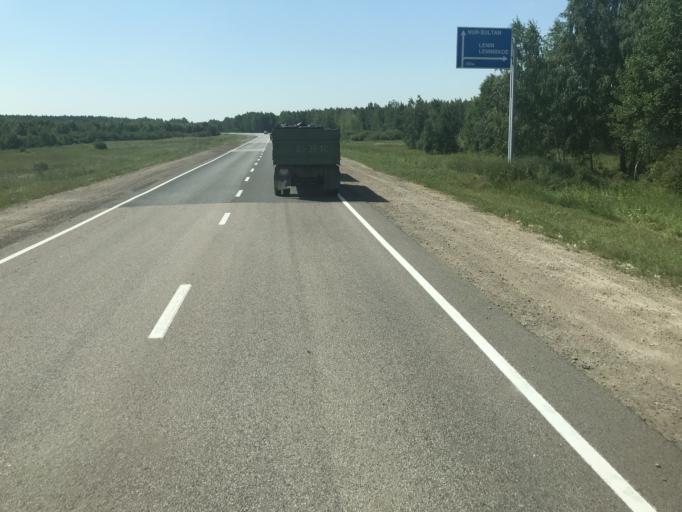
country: KZ
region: Soltustik Qazaqstan
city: Smirnovo
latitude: 54.4829
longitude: 69.2228
